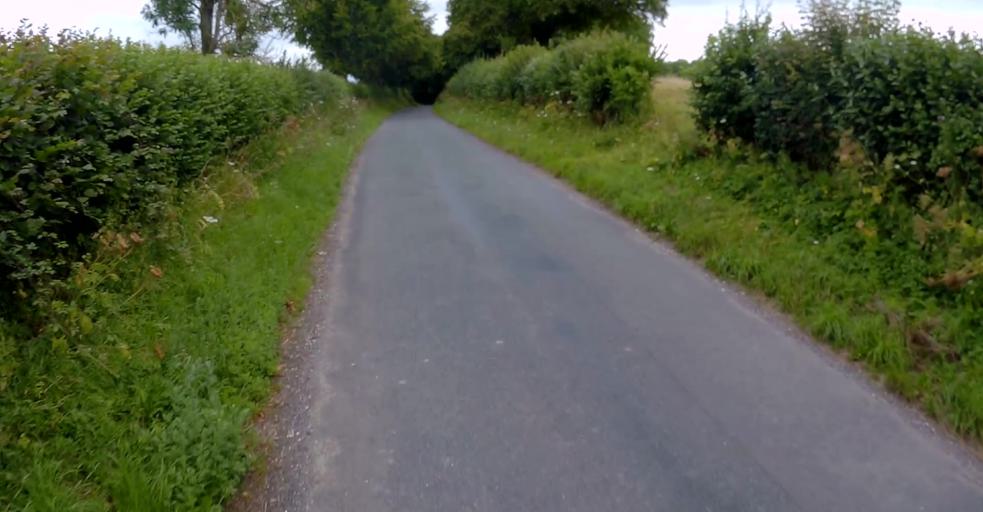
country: GB
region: England
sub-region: Hampshire
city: Kings Worthy
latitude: 51.0742
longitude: -1.2050
